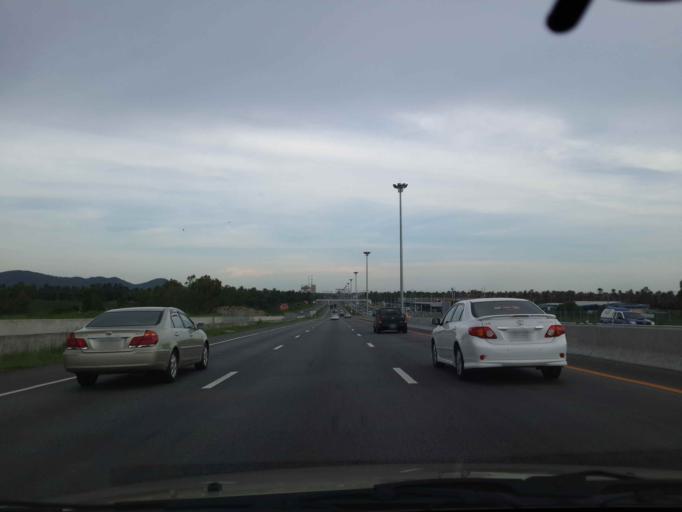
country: TH
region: Chon Buri
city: Ban Talat Bueng
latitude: 13.0283
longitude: 100.9964
